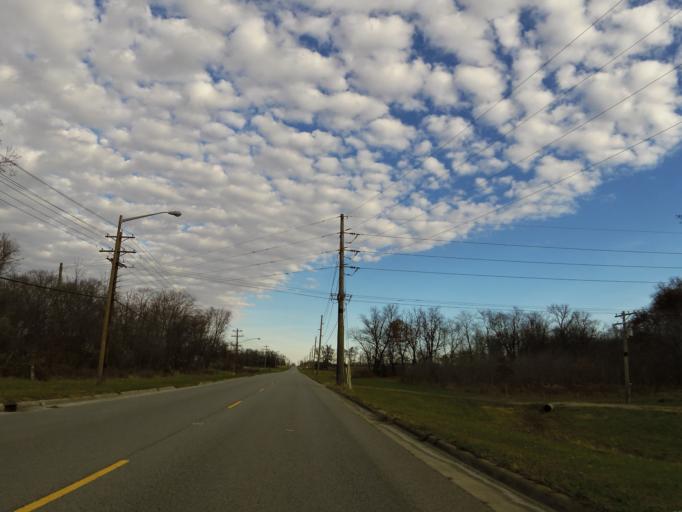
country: US
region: Illinois
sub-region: Jefferson County
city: Mount Vernon
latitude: 38.3180
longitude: -88.9700
